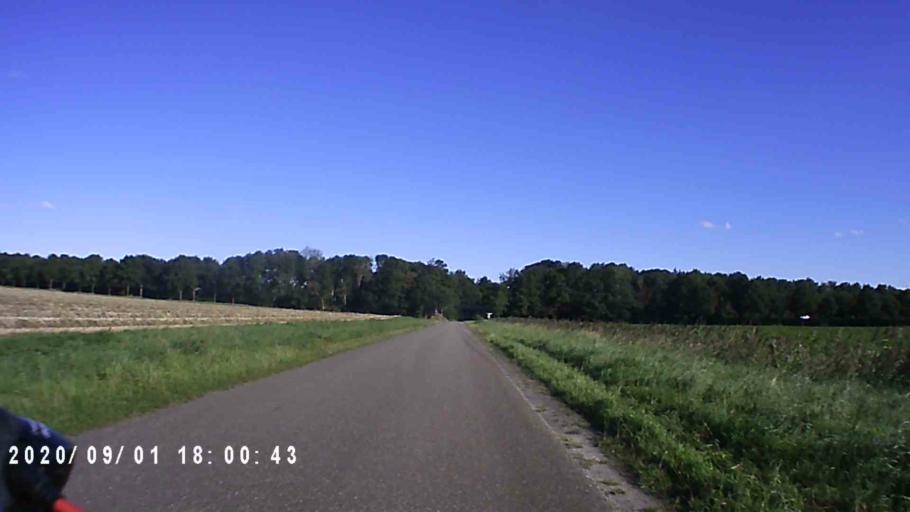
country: NL
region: Groningen
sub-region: Gemeente Slochteren
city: Slochteren
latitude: 53.2019
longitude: 6.7793
